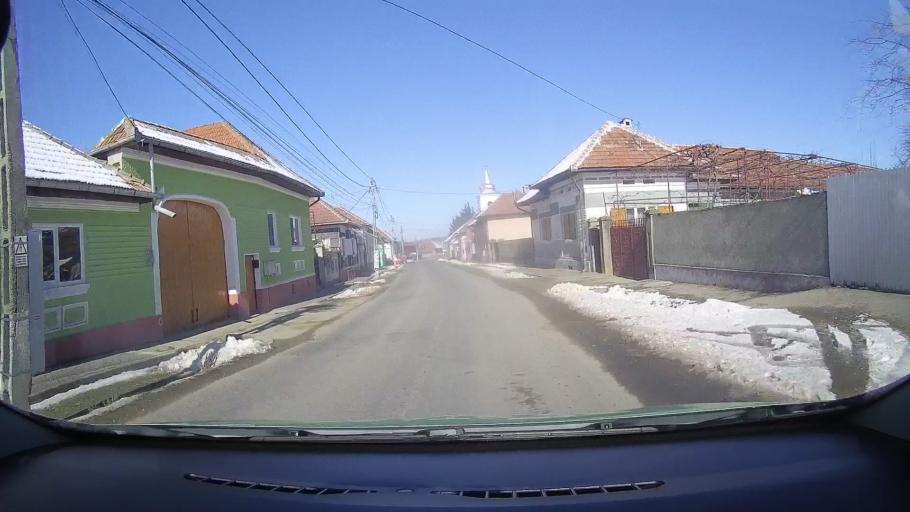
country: RO
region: Brasov
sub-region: Oras Victoria
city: Victoria
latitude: 45.7454
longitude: 24.7401
